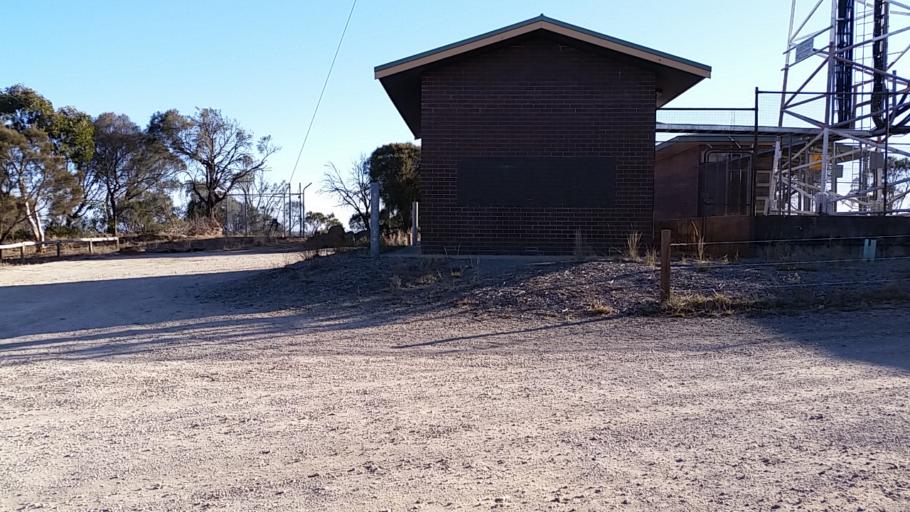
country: AU
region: South Australia
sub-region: Mount Barker
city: Nairne
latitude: -35.0666
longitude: 138.9216
